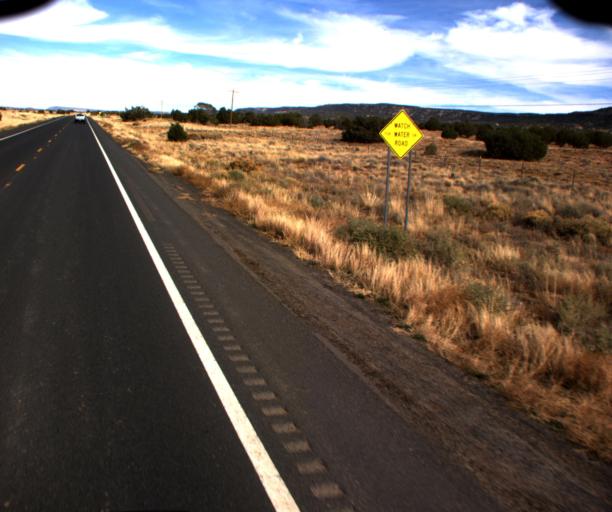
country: US
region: Arizona
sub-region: Coconino County
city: Kaibito
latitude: 36.4839
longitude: -110.6432
